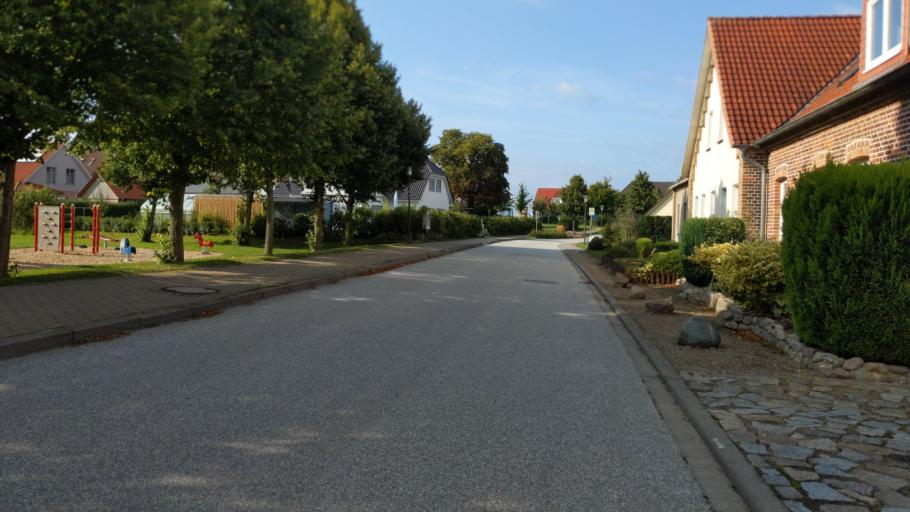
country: DE
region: Mecklenburg-Vorpommern
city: Kalkhorst
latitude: 53.9869
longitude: 11.0074
